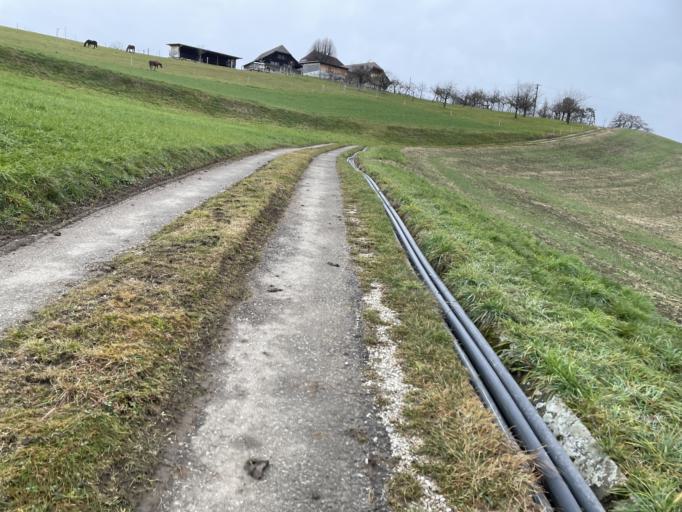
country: CH
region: Bern
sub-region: Bern-Mittelland District
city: Munsingen
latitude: 46.8650
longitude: 7.5372
